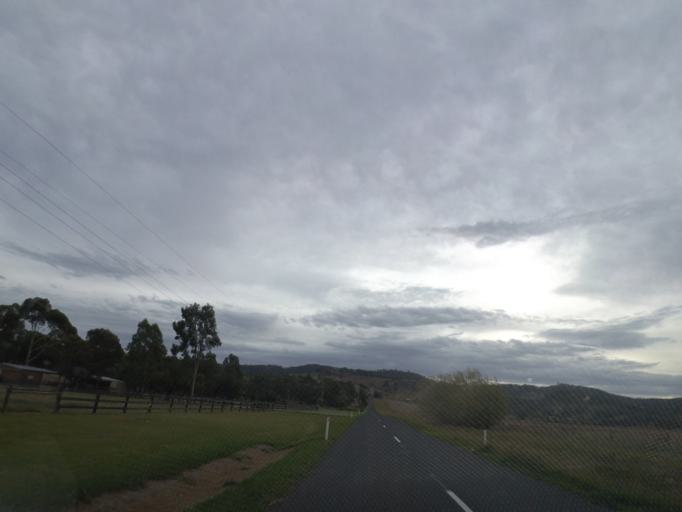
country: AU
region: Victoria
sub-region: Yarra Ranges
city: Yarra Glen
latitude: -37.6301
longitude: 145.3809
